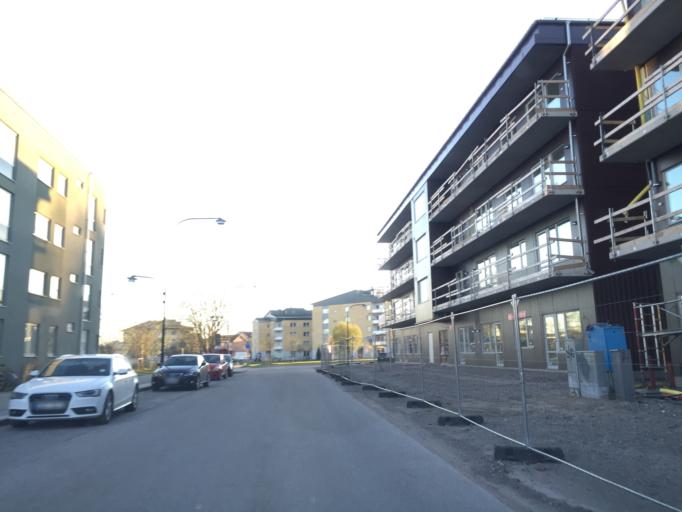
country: SE
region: OErebro
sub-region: Orebro Kommun
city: Orebro
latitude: 59.2578
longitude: 15.2164
